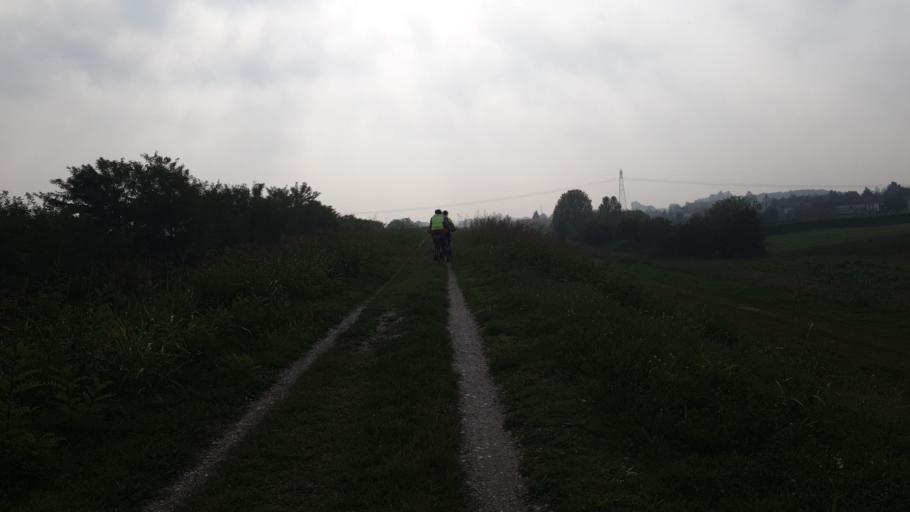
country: IT
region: Veneto
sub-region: Provincia di Venezia
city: Galta
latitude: 45.3705
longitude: 12.0286
